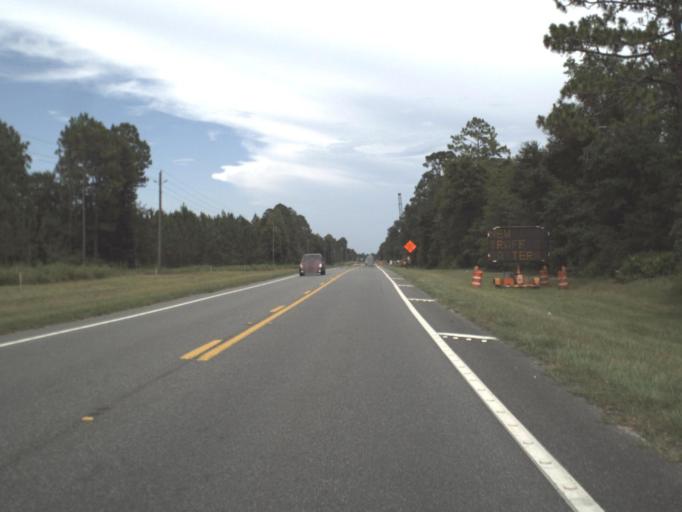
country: US
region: Florida
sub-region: Taylor County
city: Perry
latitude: 30.0976
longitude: -83.4771
